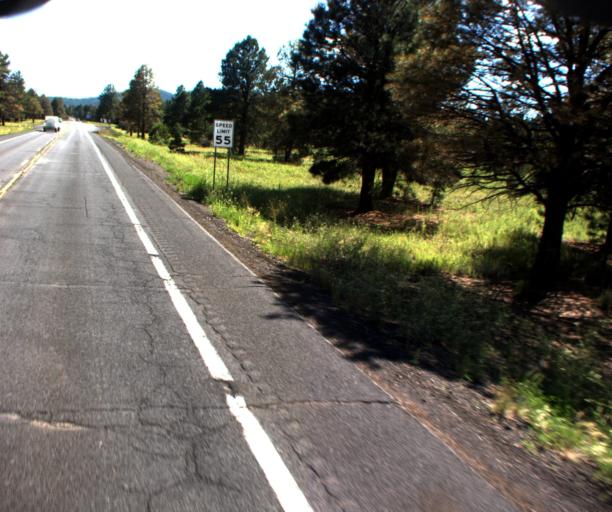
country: US
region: Arizona
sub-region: Coconino County
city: Williams
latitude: 35.2739
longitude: -112.1482
